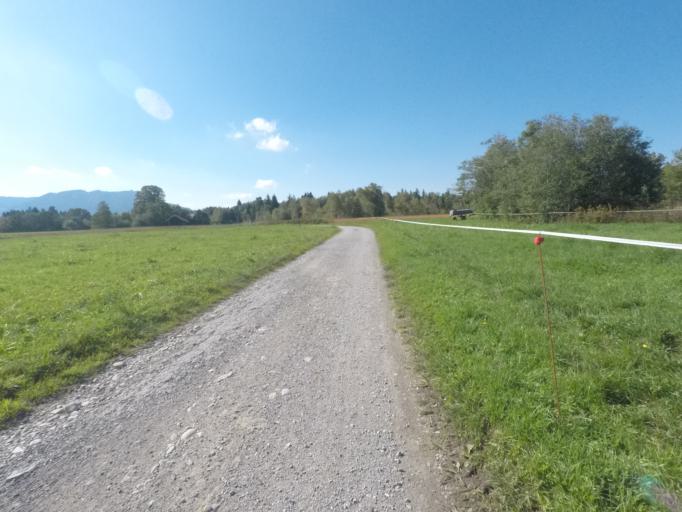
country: DE
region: Bavaria
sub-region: Upper Bavaria
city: Gaissach
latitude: 47.7427
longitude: 11.5956
